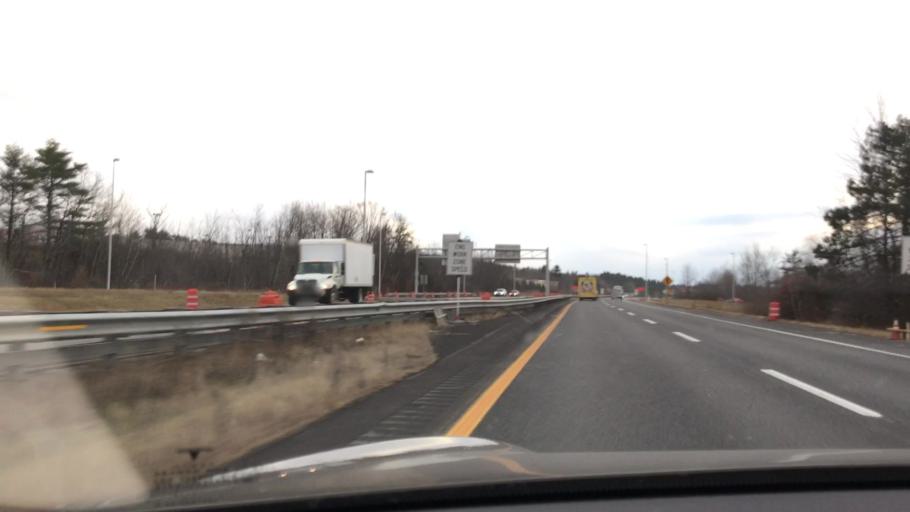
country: US
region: Maine
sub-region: Kennebec County
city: Augusta
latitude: 44.3123
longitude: -69.8097
